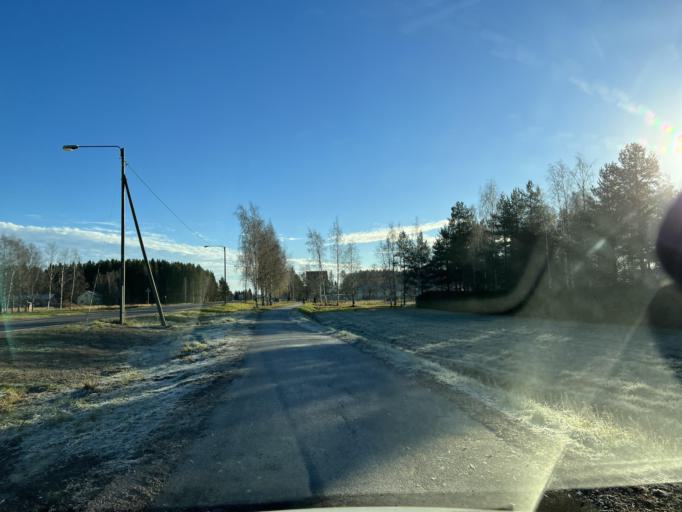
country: FI
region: Northern Ostrobothnia
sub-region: Nivala-Haapajaervi
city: Nivala
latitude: 63.9478
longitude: 24.9254
